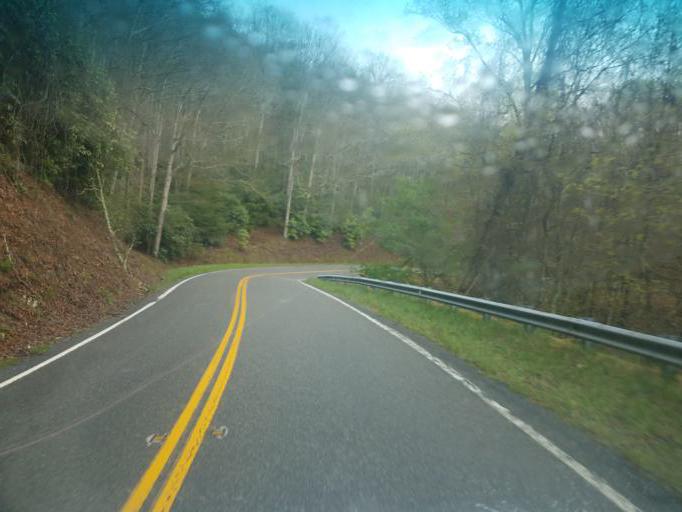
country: US
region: Virginia
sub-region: Smyth County
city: Chilhowie
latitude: 36.6551
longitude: -81.6856
